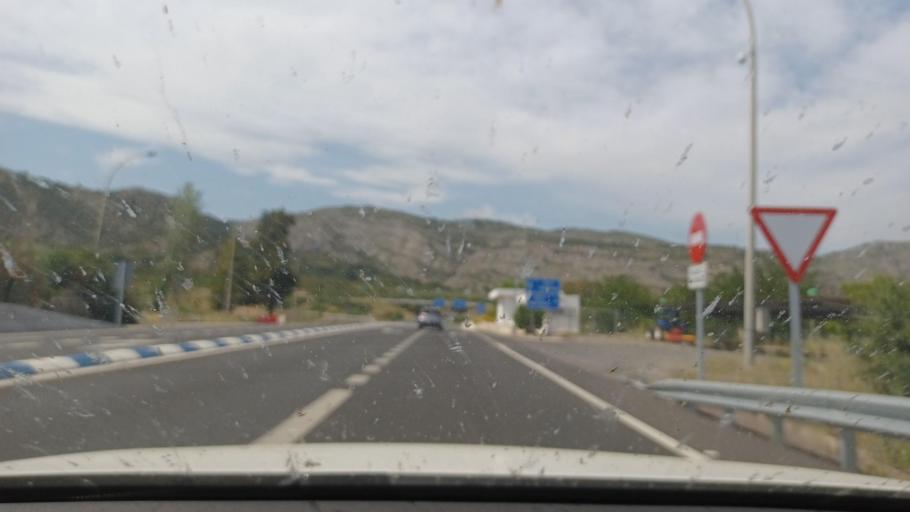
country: ES
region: Valencia
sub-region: Provincia de Castello
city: Castello de la Plana
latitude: 40.0231
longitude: -0.0294
